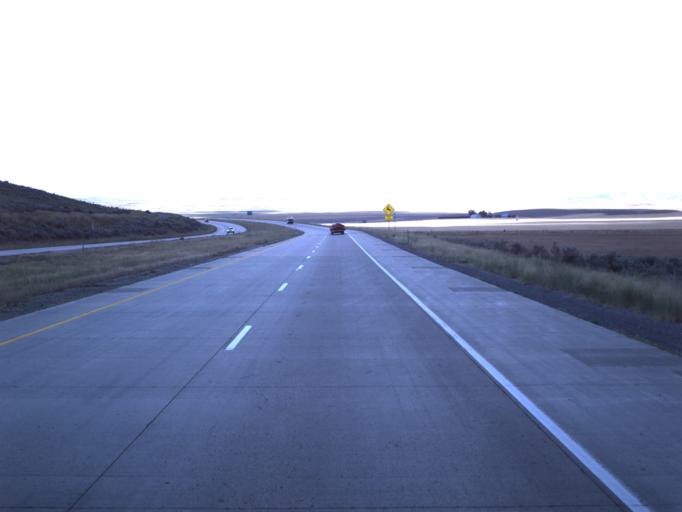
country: US
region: Utah
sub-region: Box Elder County
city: Garland
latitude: 41.8799
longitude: -112.4769
